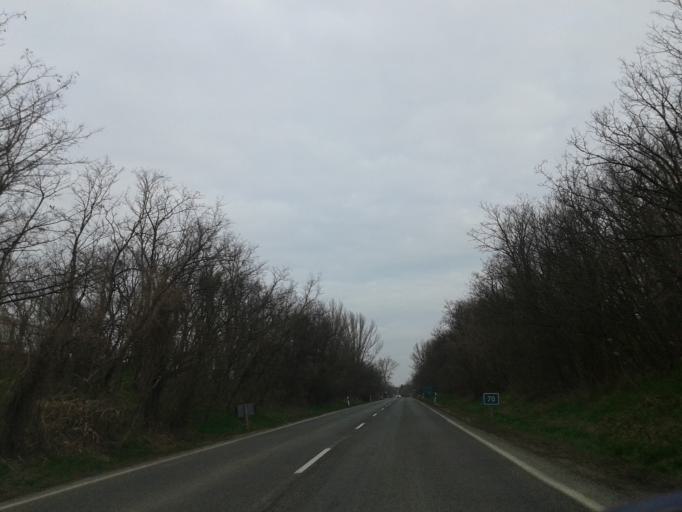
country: HU
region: Komarom-Esztergom
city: Szomod
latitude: 47.6907
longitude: 18.3099
